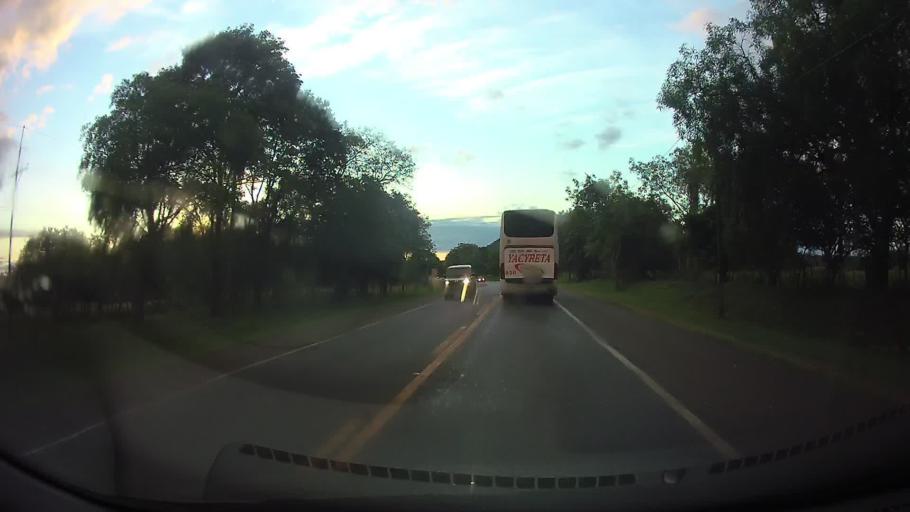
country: PY
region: Paraguari
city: Yaguaron
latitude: -25.5748
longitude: -57.2705
